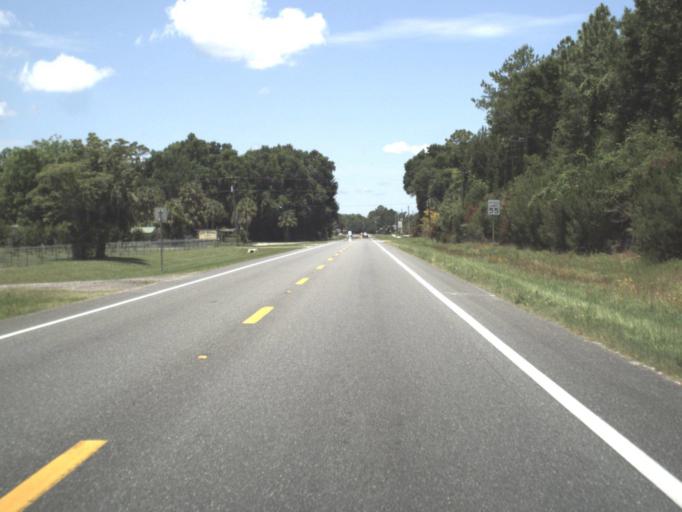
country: US
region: Florida
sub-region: Lafayette County
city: Mayo
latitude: 29.9550
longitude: -82.9134
